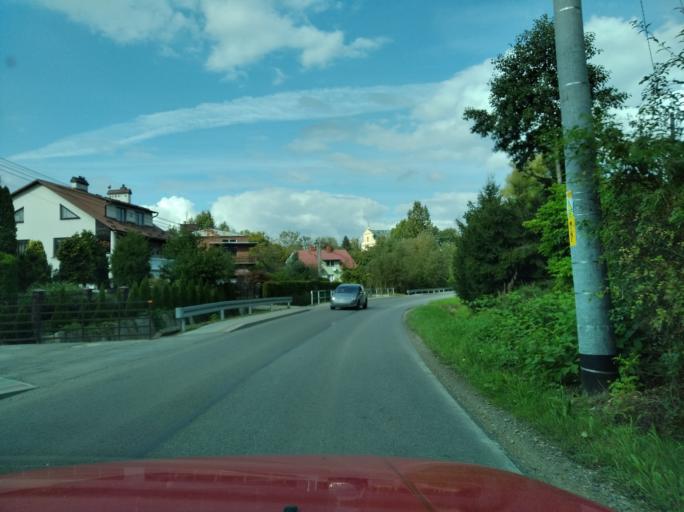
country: PL
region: Subcarpathian Voivodeship
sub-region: Powiat rzeszowski
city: Tyczyn
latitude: 49.9590
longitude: 22.0328
